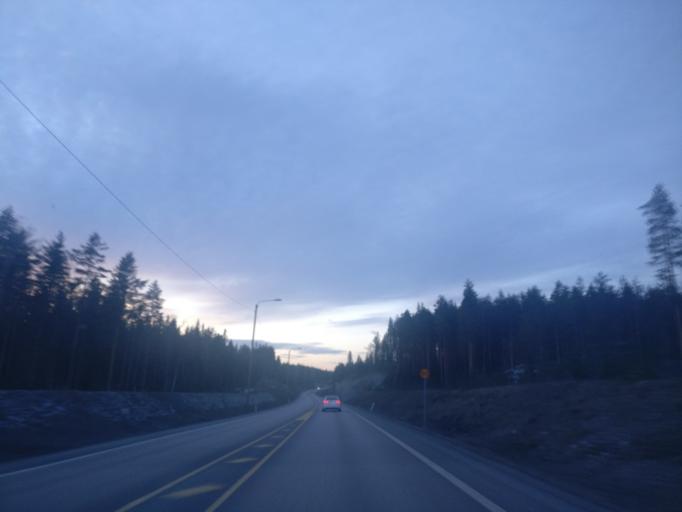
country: FI
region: Central Finland
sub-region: Jyvaeskylae
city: Saeynaetsalo
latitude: 62.1925
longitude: 25.8997
